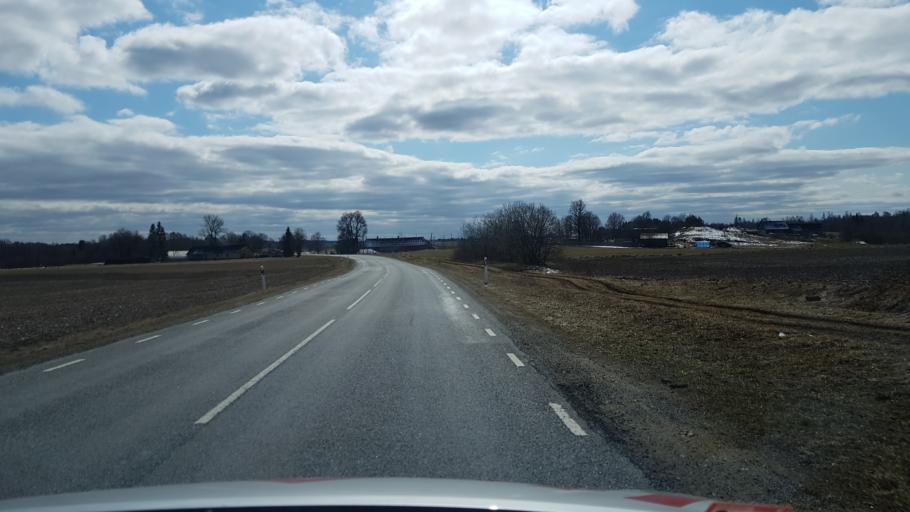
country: EE
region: Laeaene-Virumaa
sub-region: Tapa vald
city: Tapa
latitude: 59.3303
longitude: 26.0002
